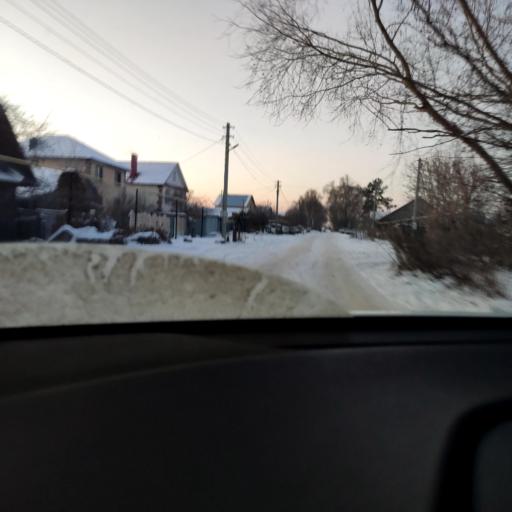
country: RU
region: Tatarstan
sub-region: Gorod Kazan'
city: Kazan
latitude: 55.7433
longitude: 49.0996
